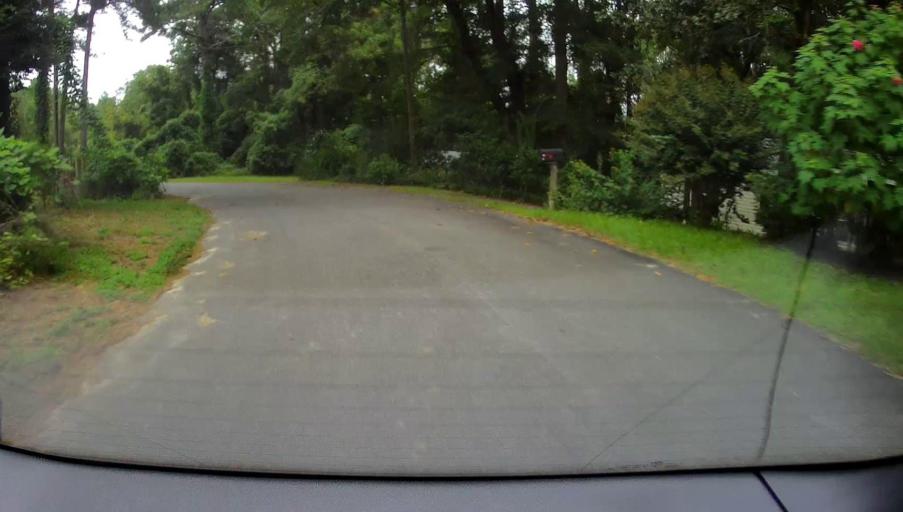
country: US
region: Georgia
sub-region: Houston County
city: Centerville
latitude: 32.6759
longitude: -83.7125
